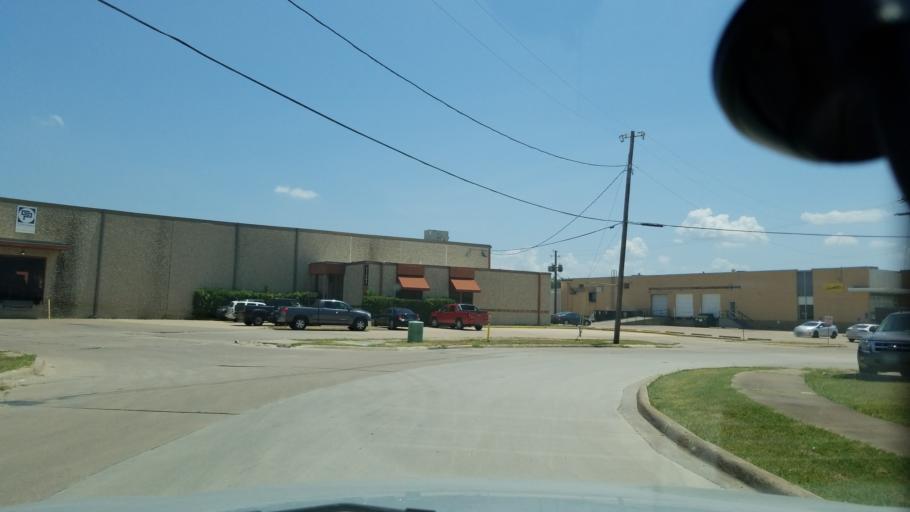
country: US
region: Texas
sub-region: Dallas County
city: Farmers Branch
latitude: 32.8935
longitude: -96.8867
